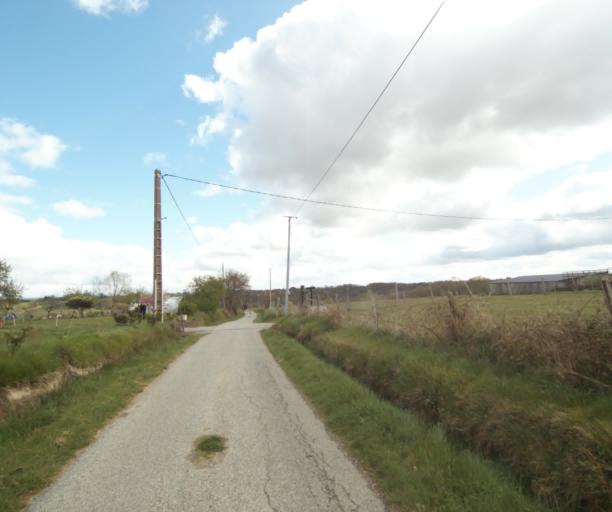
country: FR
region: Midi-Pyrenees
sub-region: Departement de l'Ariege
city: Saverdun
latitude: 43.2096
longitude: 1.5695
